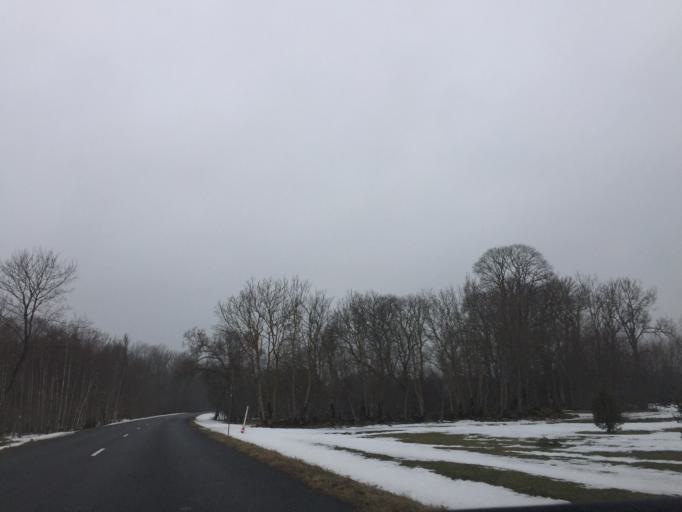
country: EE
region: Saare
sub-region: Orissaare vald
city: Orissaare
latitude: 58.3922
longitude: 22.8346
